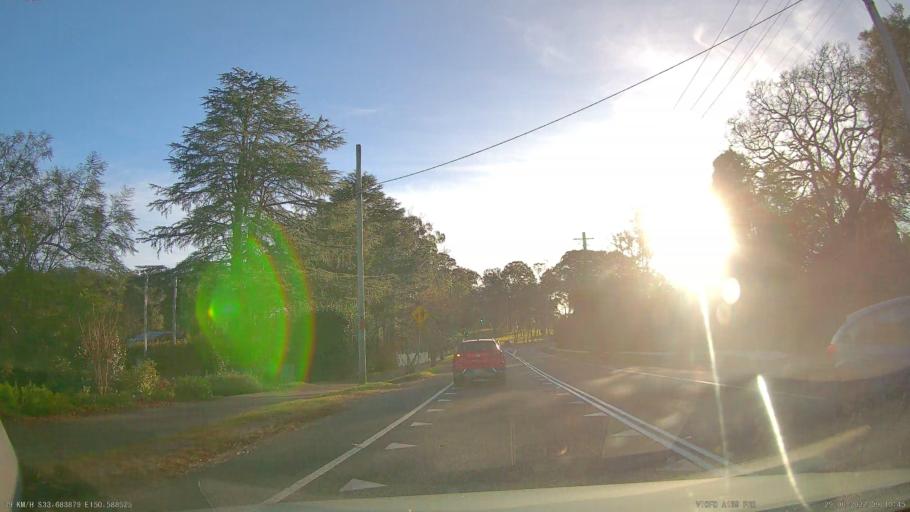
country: AU
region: New South Wales
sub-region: Blue Mountains Municipality
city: Blaxland
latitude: -33.6836
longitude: 150.5887
